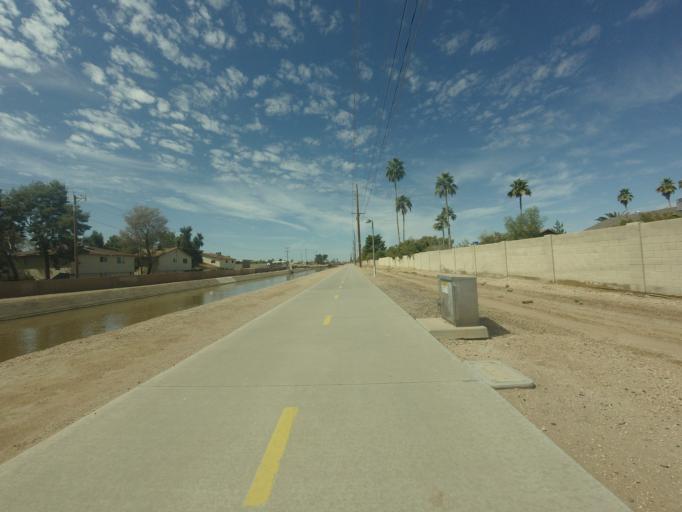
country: US
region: Arizona
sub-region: Maricopa County
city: Mesa
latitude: 33.4370
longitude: -111.8114
